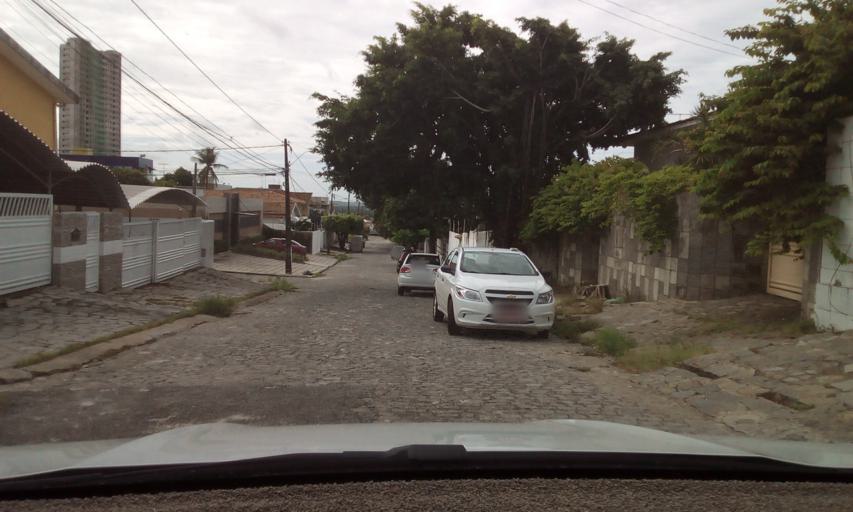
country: BR
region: Paraiba
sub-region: Joao Pessoa
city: Joao Pessoa
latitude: -7.1084
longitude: -34.8527
